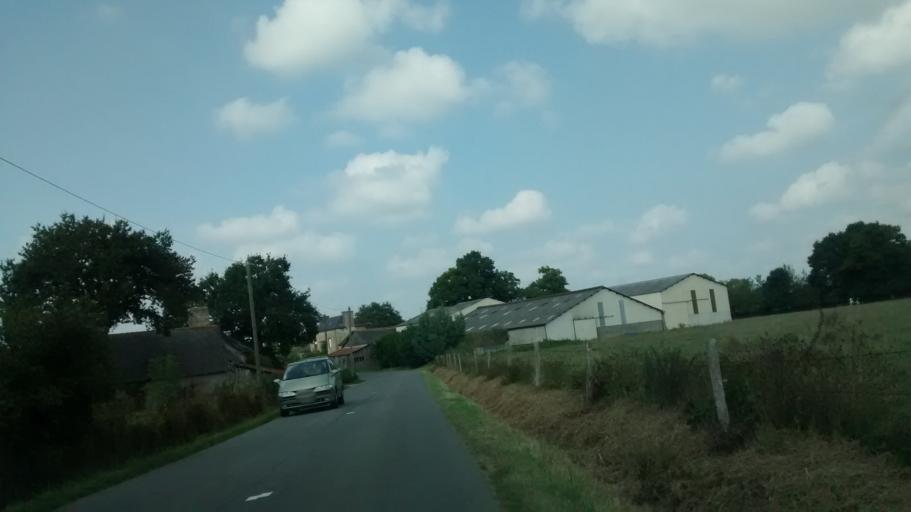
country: FR
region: Brittany
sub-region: Departement d'Ille-et-Vilaine
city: Livre-sur-Changeon
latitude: 48.2317
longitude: -1.2853
